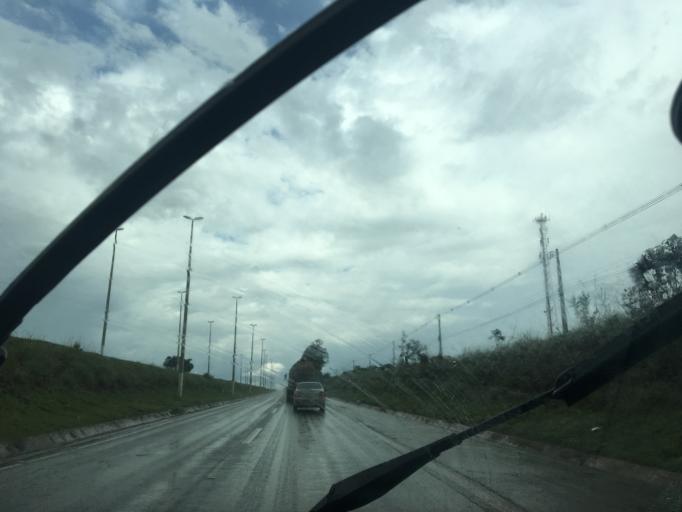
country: BR
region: Goias
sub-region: Luziania
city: Luziania
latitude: -16.1937
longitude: -47.9254
